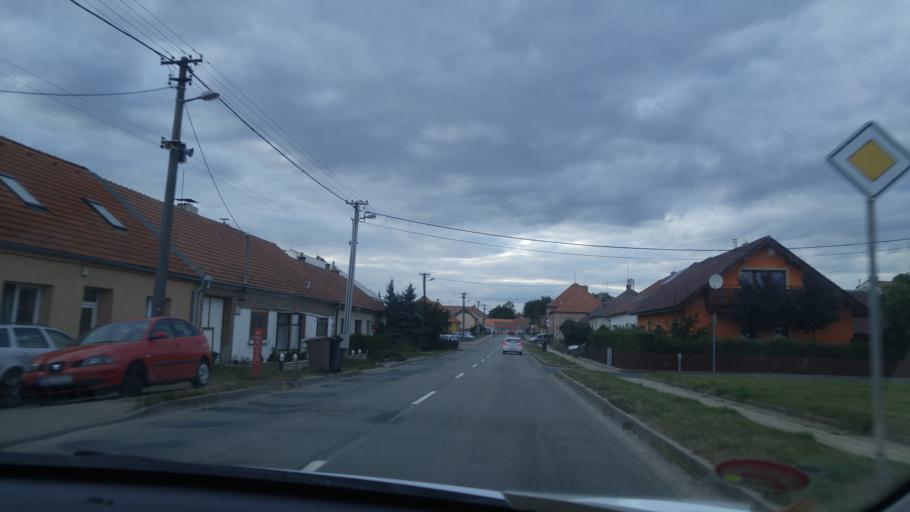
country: CZ
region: South Moravian
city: Ricany
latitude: 49.2080
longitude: 16.4138
